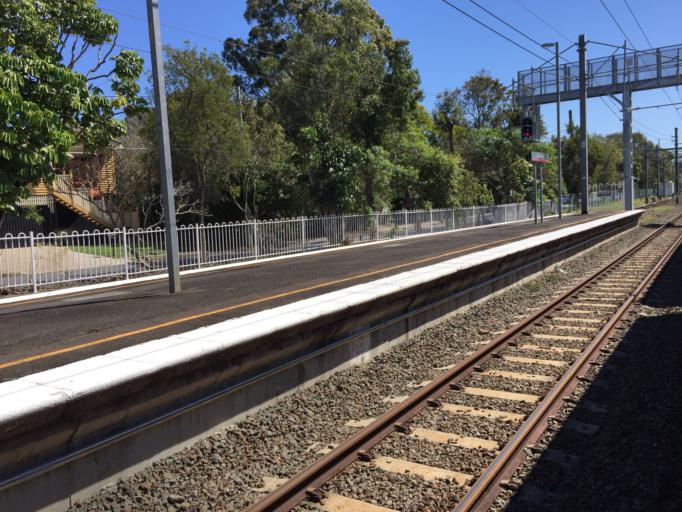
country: AU
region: Queensland
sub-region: Brisbane
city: Rocklea
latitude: -27.5306
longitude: 152.9793
